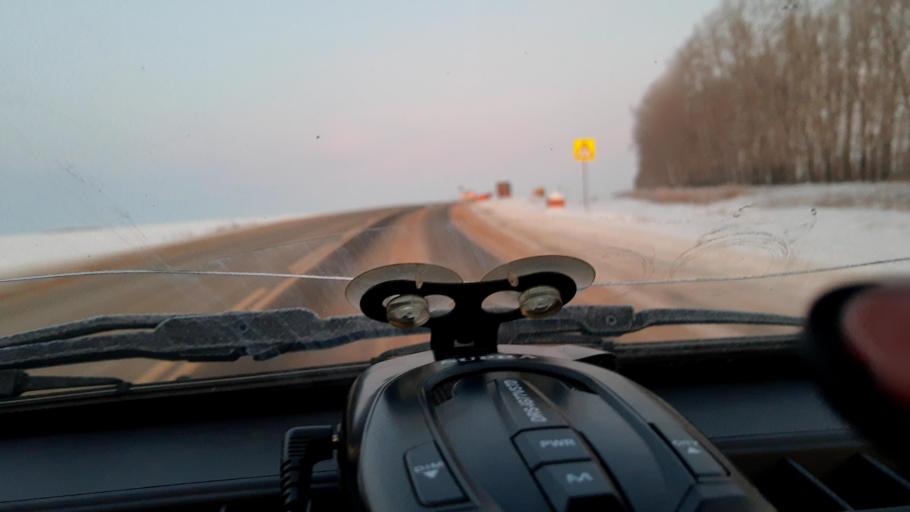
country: RU
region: Bashkortostan
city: Blagoveshchensk
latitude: 55.0854
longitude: 55.8585
